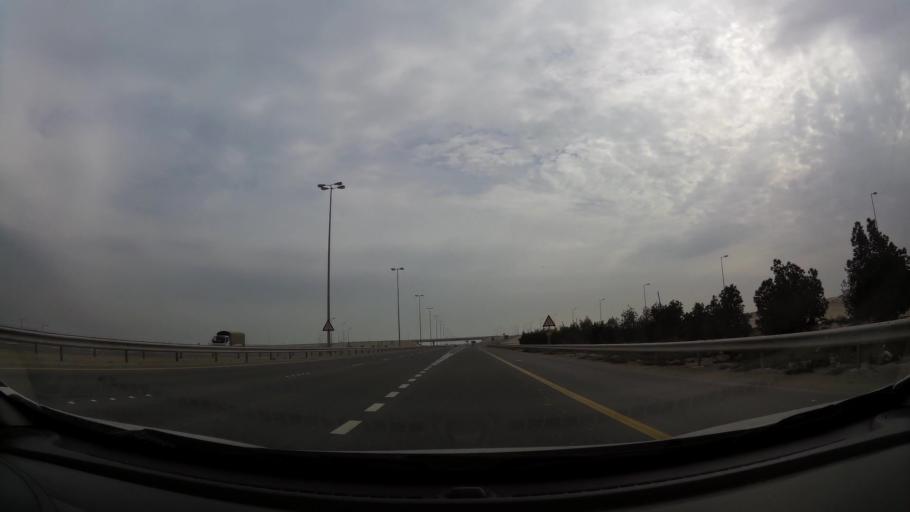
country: BH
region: Northern
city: Ar Rifa'
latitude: 26.0525
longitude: 50.6067
